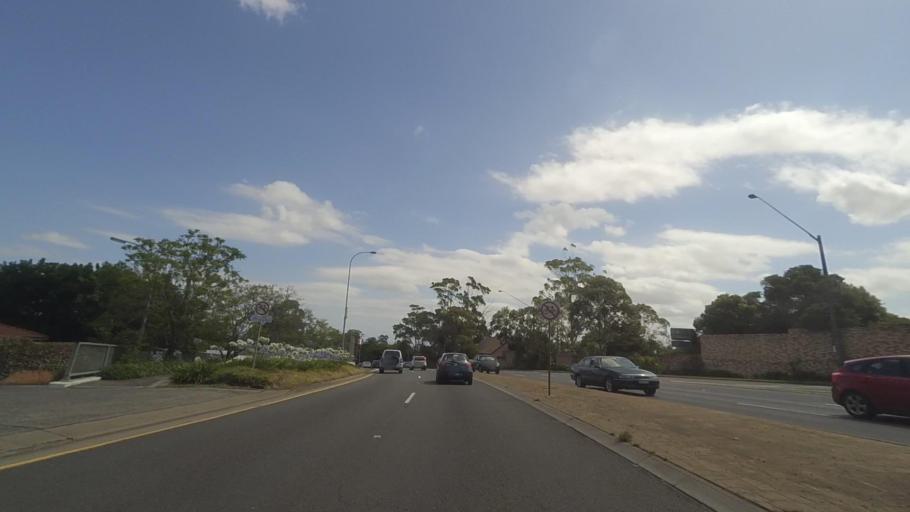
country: AU
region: New South Wales
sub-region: The Hills Shire
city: West Pennant
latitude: -33.7484
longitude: 151.0497
